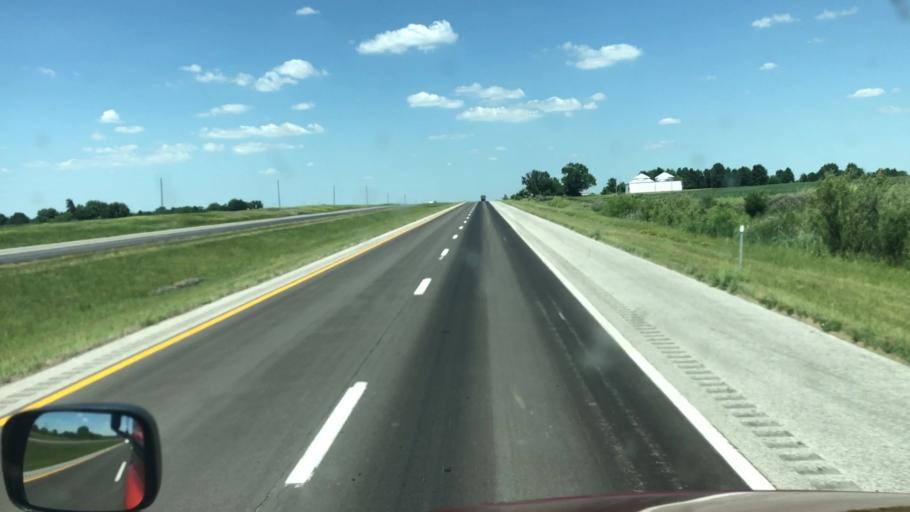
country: US
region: Missouri
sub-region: Macon County
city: La Plata
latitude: 40.0024
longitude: -92.4751
